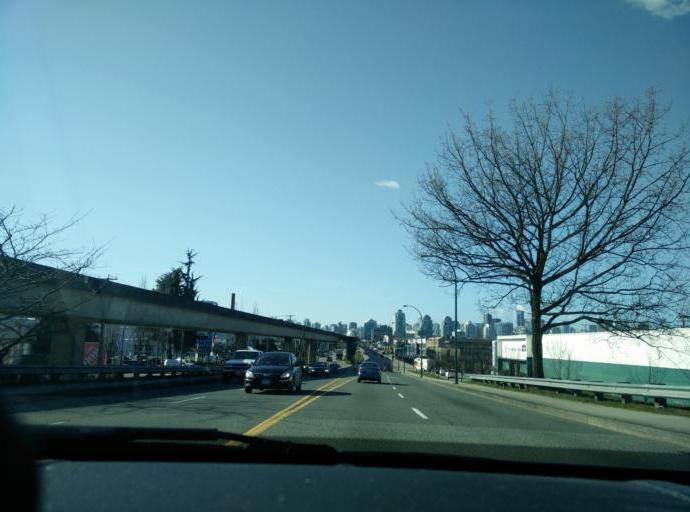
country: CA
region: British Columbia
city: Vancouver
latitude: 49.2700
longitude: -123.0827
